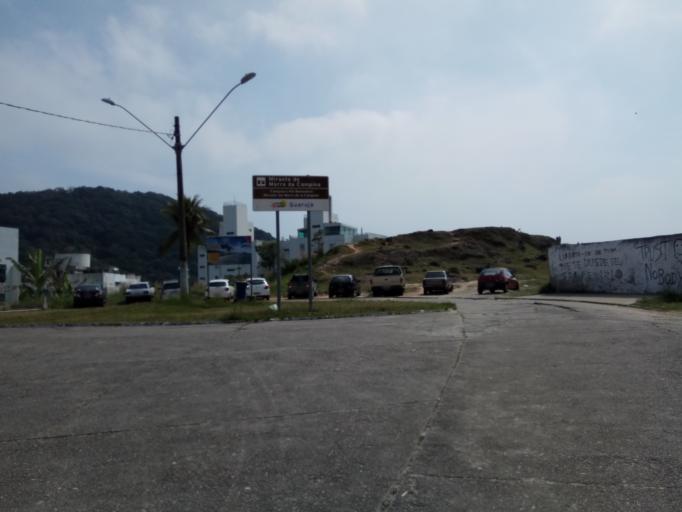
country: BR
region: Sao Paulo
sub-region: Guaruja
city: Guaruja
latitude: -23.9951
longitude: -46.2490
